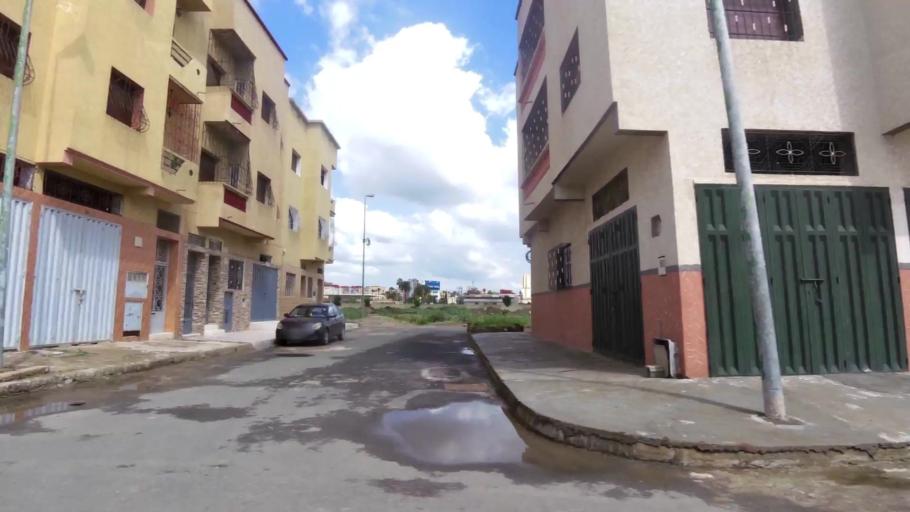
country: MA
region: Chaouia-Ouardigha
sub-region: Settat Province
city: Berrechid
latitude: 33.2596
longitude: -7.5948
